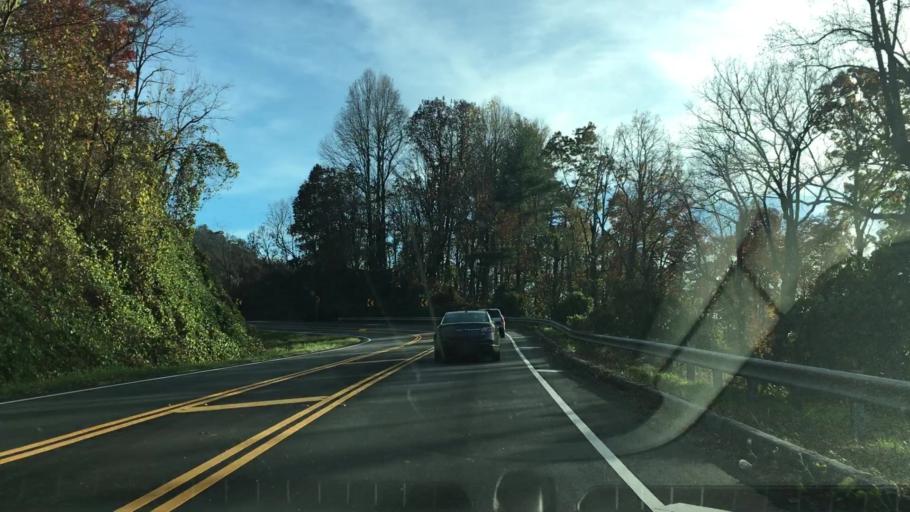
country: US
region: Georgia
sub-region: Rabun County
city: Mountain City
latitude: 34.9959
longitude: -83.3533
